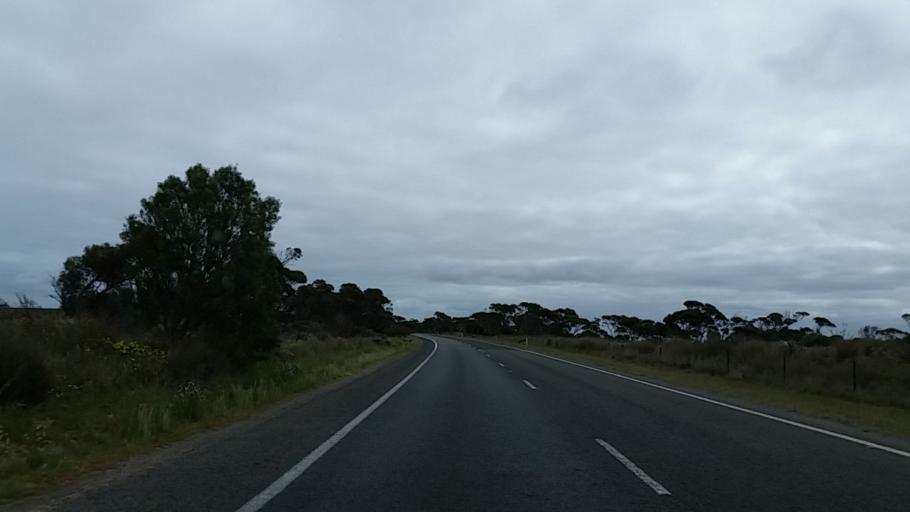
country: AU
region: South Australia
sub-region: Wakefield
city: Balaklava
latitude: -34.3332
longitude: 138.2759
